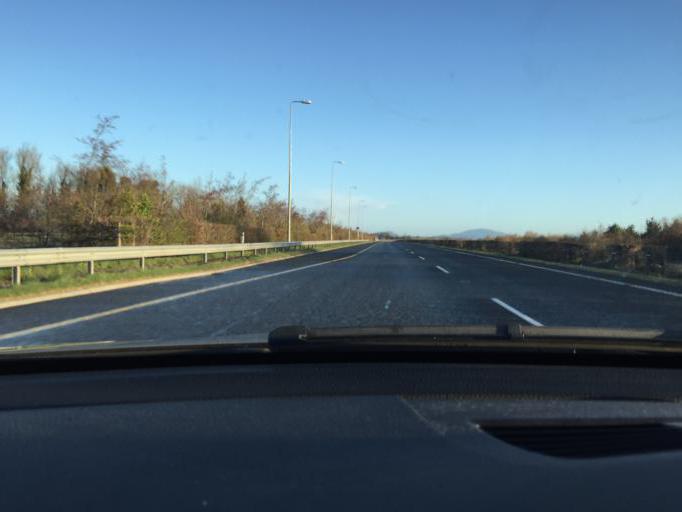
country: IE
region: Leinster
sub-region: Lu
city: Dromiskin
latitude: 53.9369
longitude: -6.4159
